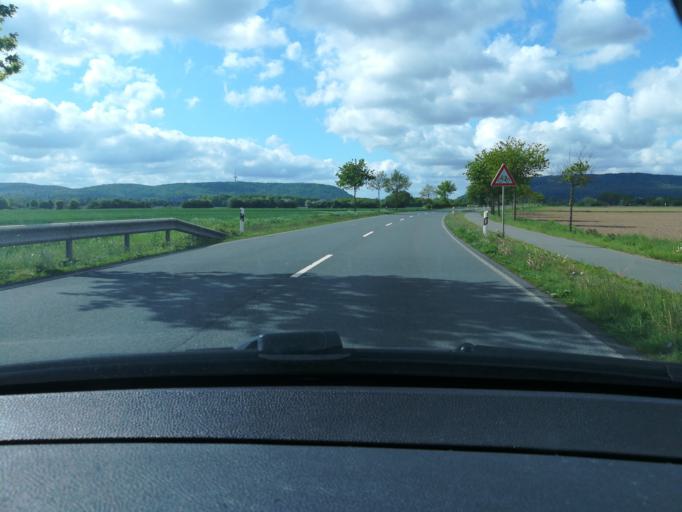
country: DE
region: North Rhine-Westphalia
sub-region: Regierungsbezirk Detmold
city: Minden
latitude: 52.2824
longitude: 8.9298
